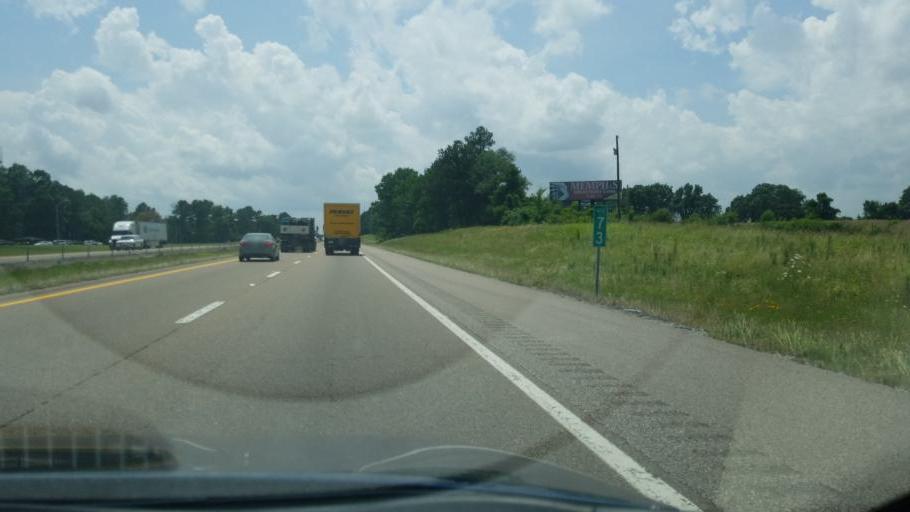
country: US
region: Tennessee
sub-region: Crockett County
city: Bells
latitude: 35.6252
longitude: -88.9758
